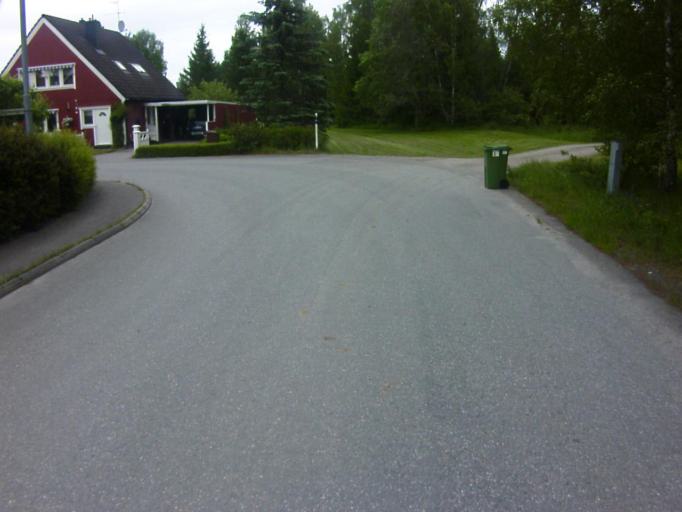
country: SE
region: Soedermanland
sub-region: Eskilstuna Kommun
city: Skogstorp
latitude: 59.3179
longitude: 16.4813
